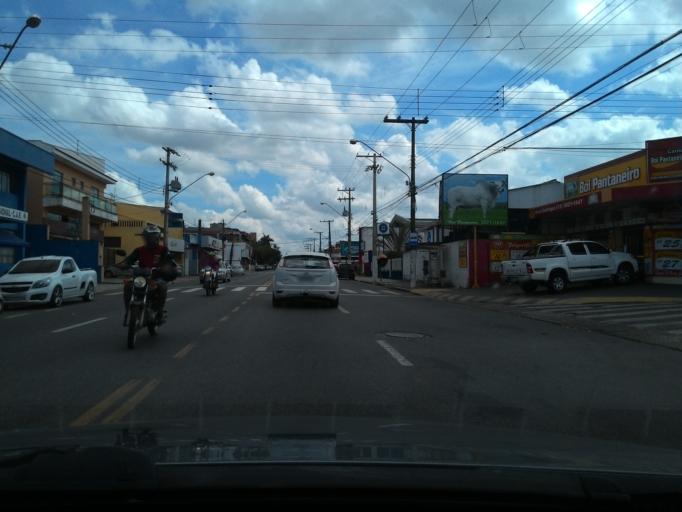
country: BR
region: Sao Paulo
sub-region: Registro
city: Registro
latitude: -24.4985
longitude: -47.8506
